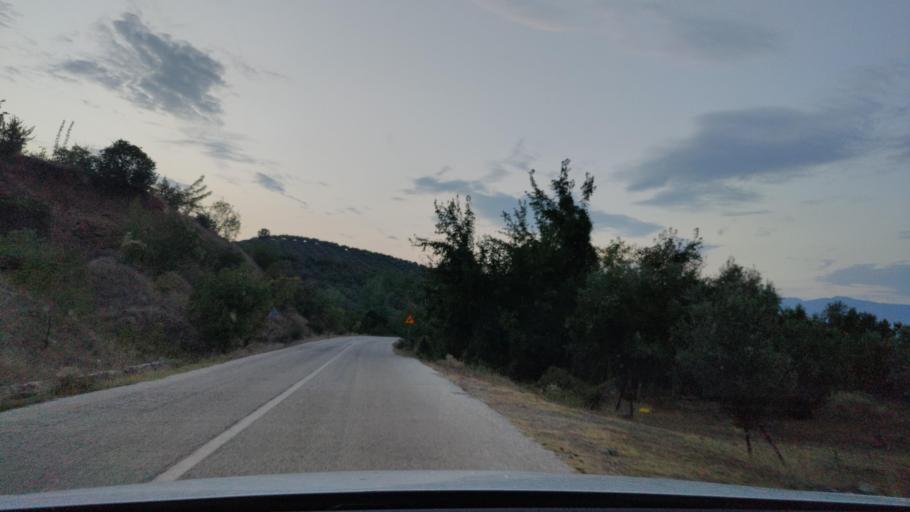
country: GR
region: Central Macedonia
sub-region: Nomos Serron
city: Chrysochorafa
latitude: 41.1434
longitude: 23.2132
